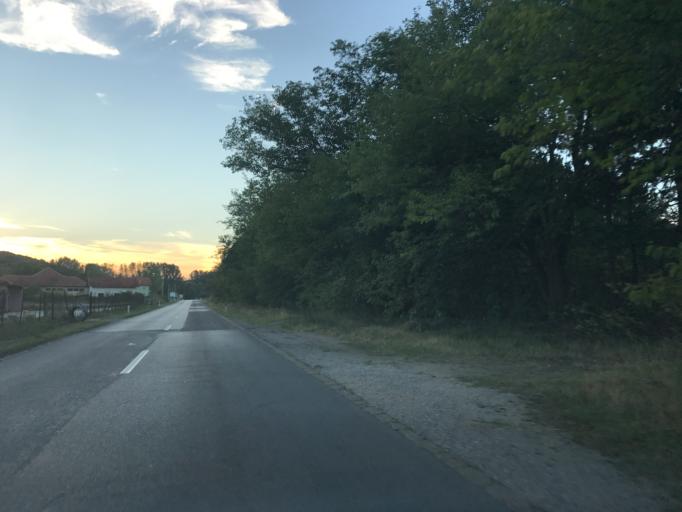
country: RS
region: Central Serbia
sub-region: Branicevski Okrug
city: Golubac
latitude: 44.6731
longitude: 21.6023
